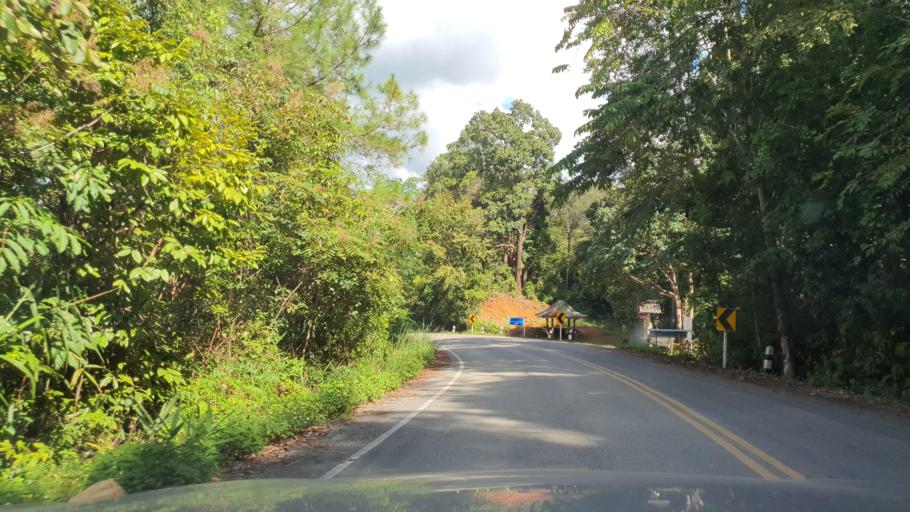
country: TH
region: Chiang Rai
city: Wiang Pa Pao
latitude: 19.3030
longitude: 99.3699
